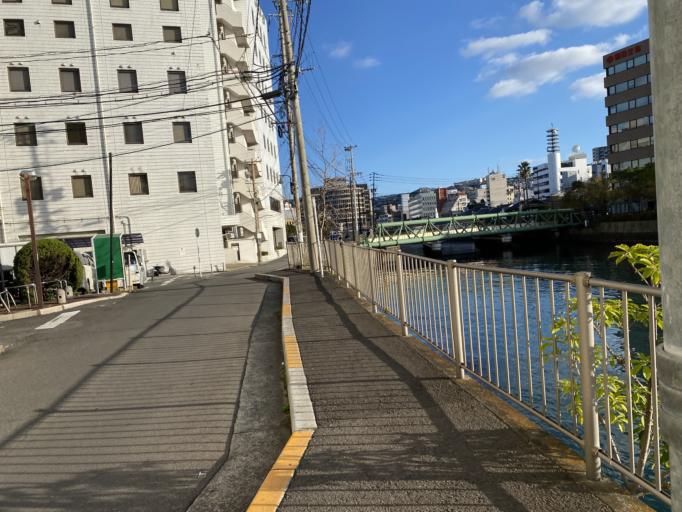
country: JP
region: Nagasaki
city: Nagasaki-shi
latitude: 32.7454
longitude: 129.8710
